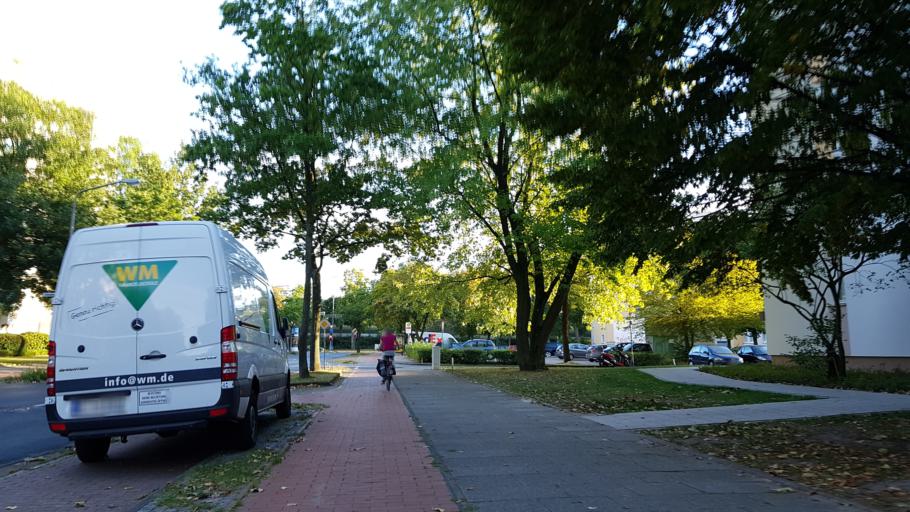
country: DE
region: Lower Saxony
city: Riede
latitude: 53.0403
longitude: 8.9320
